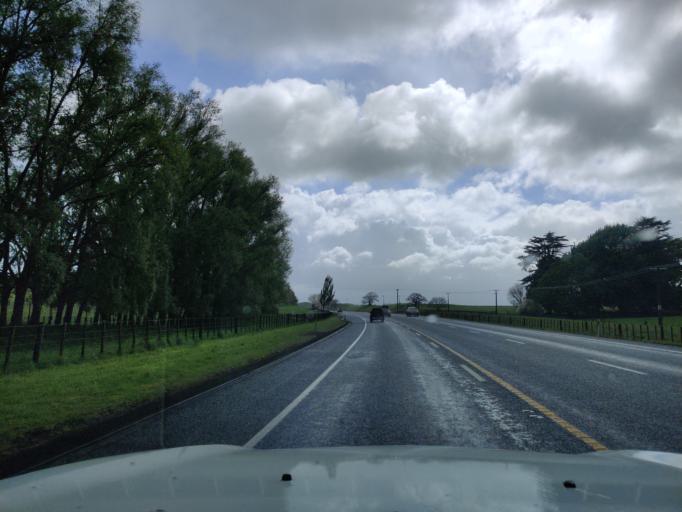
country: NZ
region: Waikato
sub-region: Matamata-Piako District
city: Matamata
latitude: -37.9835
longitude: 175.7335
